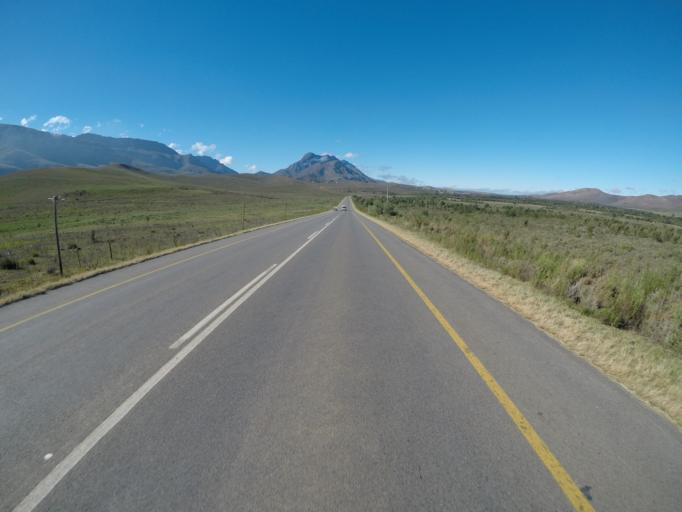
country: ZA
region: Western Cape
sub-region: Overberg District Municipality
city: Caledon
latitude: -34.0491
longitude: 19.5733
